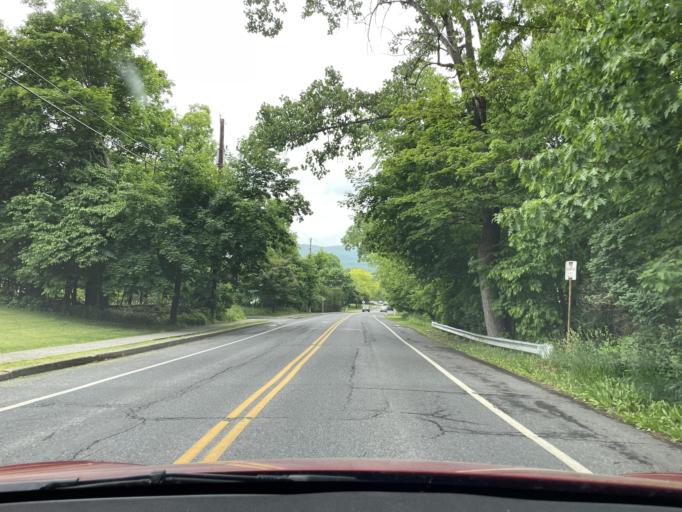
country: US
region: New York
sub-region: Ulster County
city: New Paltz
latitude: 41.7516
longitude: -74.0810
